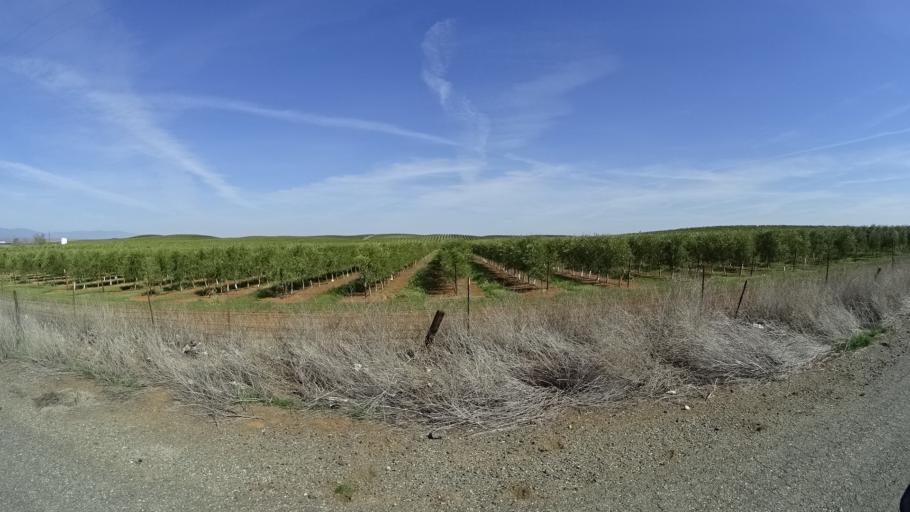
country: US
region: California
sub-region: Glenn County
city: Willows
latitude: 39.6114
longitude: -122.2858
